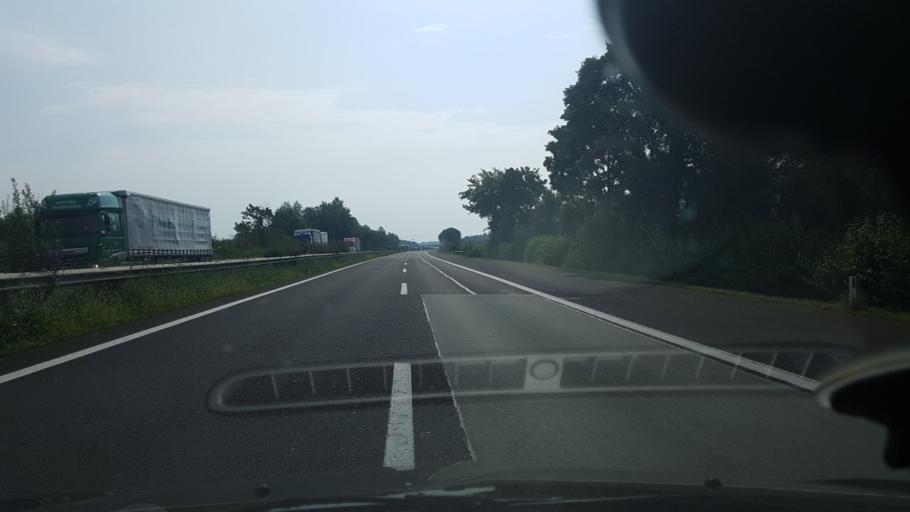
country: AT
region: Styria
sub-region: Politischer Bezirk Hartberg-Fuerstenfeld
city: Ilz
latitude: 47.0799
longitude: 15.9258
